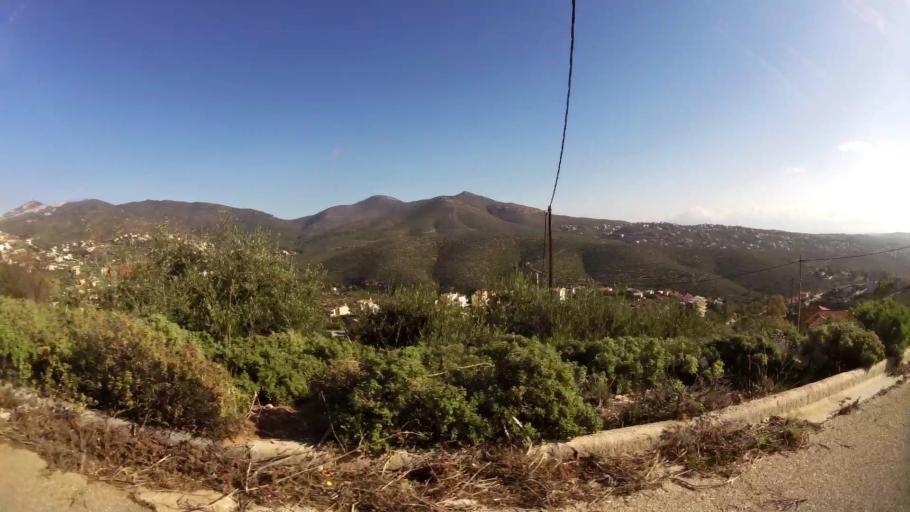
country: GR
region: Attica
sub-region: Nomarchia Anatolikis Attikis
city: Dhrafi
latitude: 38.0254
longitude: 23.9014
